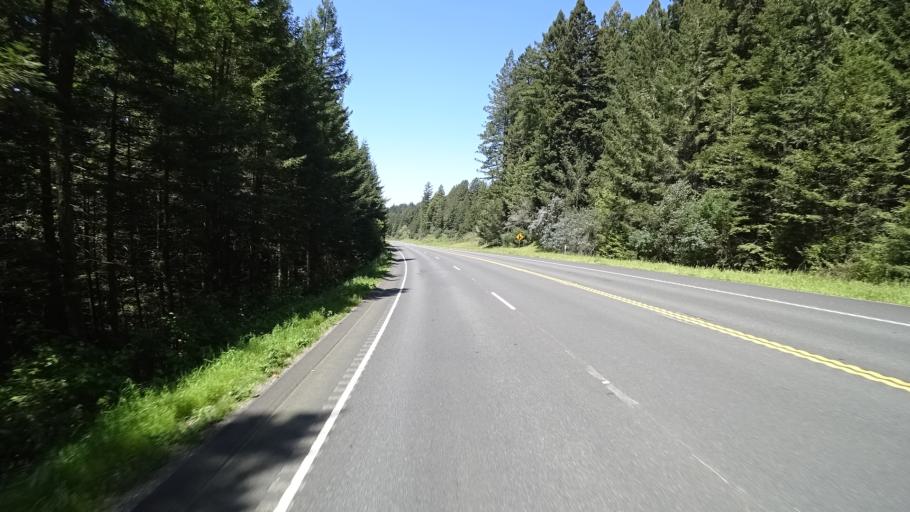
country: US
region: California
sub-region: Humboldt County
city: Blue Lake
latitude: 40.8867
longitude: -123.9725
